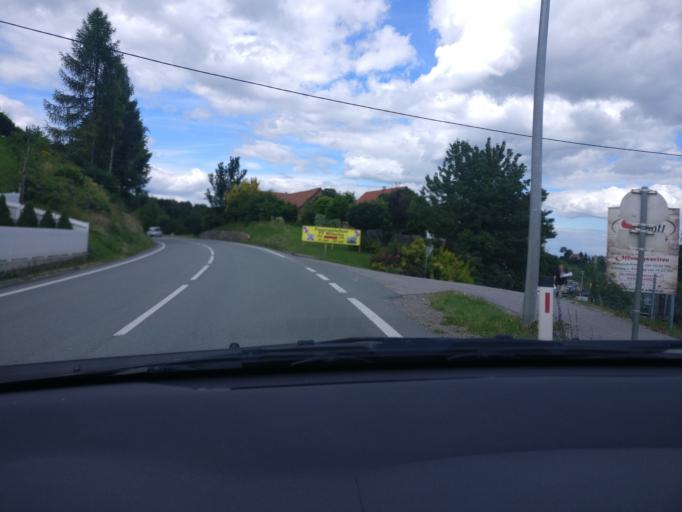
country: AT
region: Styria
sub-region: Politischer Bezirk Weiz
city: Nitscha
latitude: 47.1334
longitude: 15.7305
